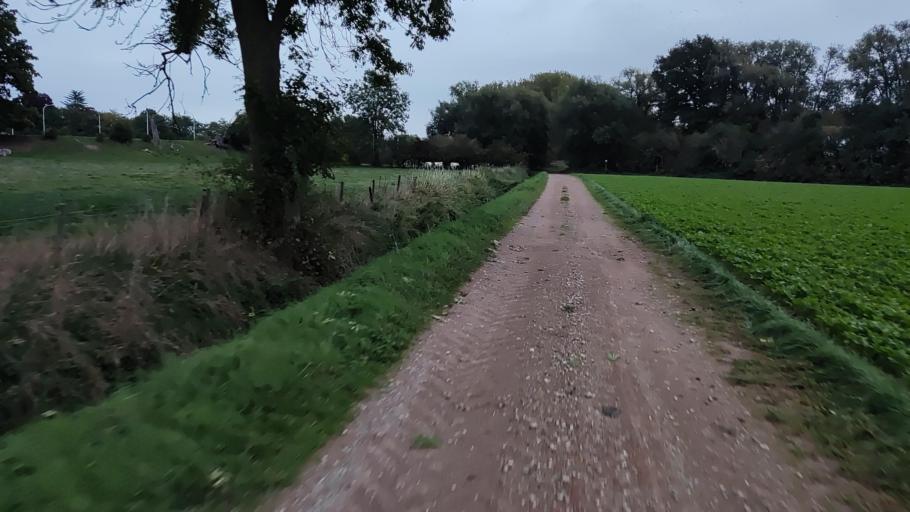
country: BE
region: Flanders
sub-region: Provincie Vlaams-Brabant
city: Tienen
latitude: 50.7876
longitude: 4.9227
